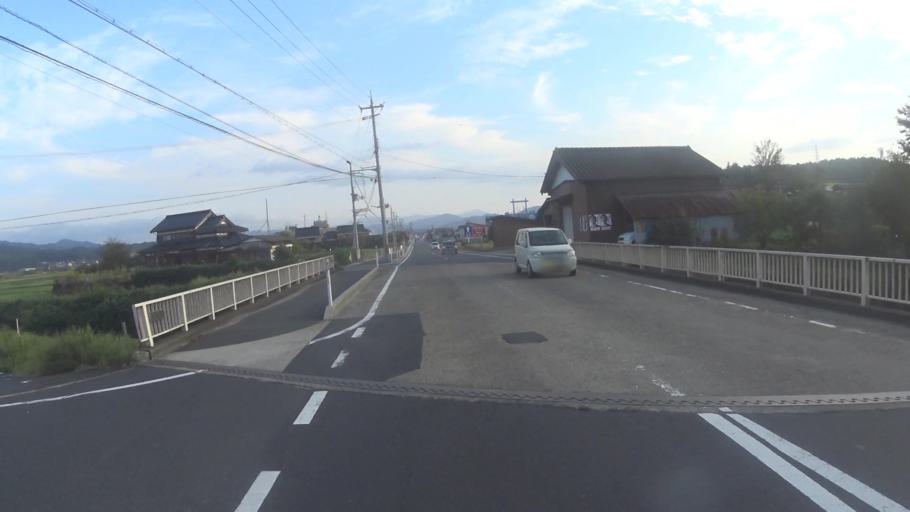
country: JP
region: Kyoto
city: Miyazu
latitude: 35.6281
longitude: 135.0720
